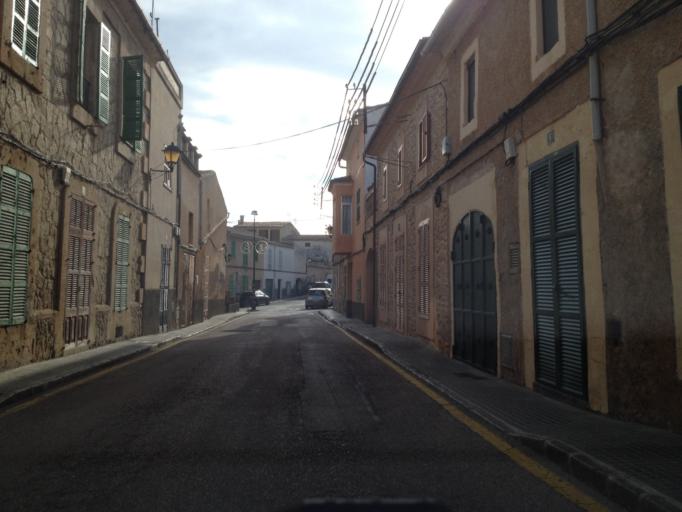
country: ES
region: Balearic Islands
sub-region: Illes Balears
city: Son Servera
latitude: 39.6242
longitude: 3.3569
